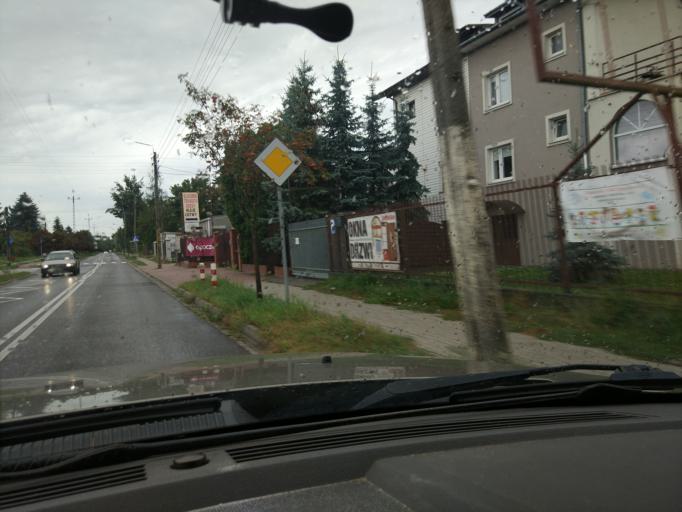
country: PL
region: Masovian Voivodeship
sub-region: Powiat pruszkowski
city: Brwinow
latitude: 52.1348
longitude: 20.7175
